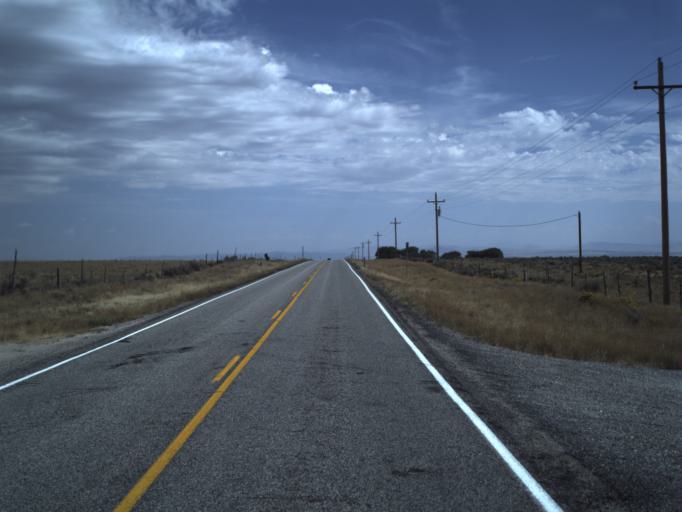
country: US
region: Idaho
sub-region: Cassia County
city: Burley
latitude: 41.8171
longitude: -113.2909
